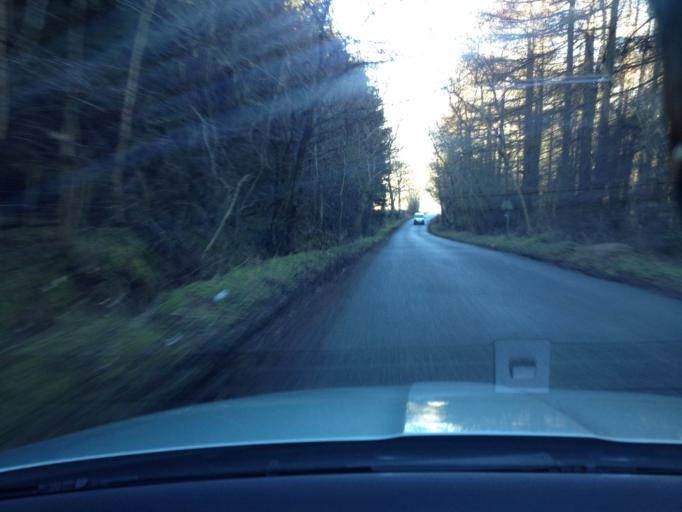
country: GB
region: Scotland
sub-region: Perth and Kinross
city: Bridge of Earn
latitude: 56.3177
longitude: -3.3698
